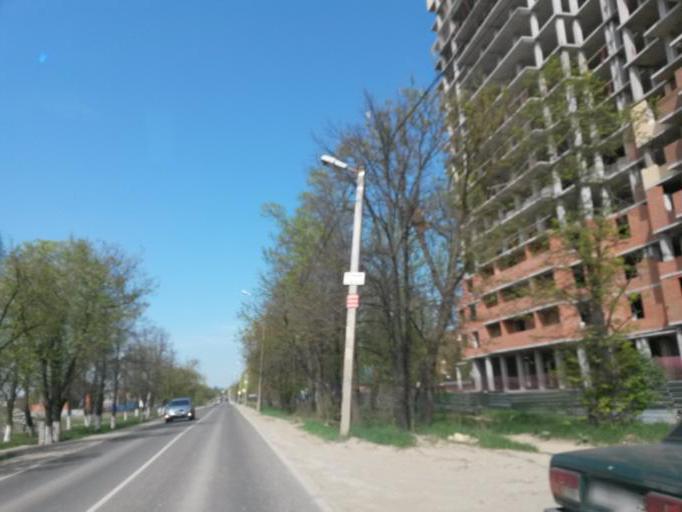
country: RU
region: Moskovskaya
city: Klimovsk
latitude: 55.3527
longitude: 37.5401
